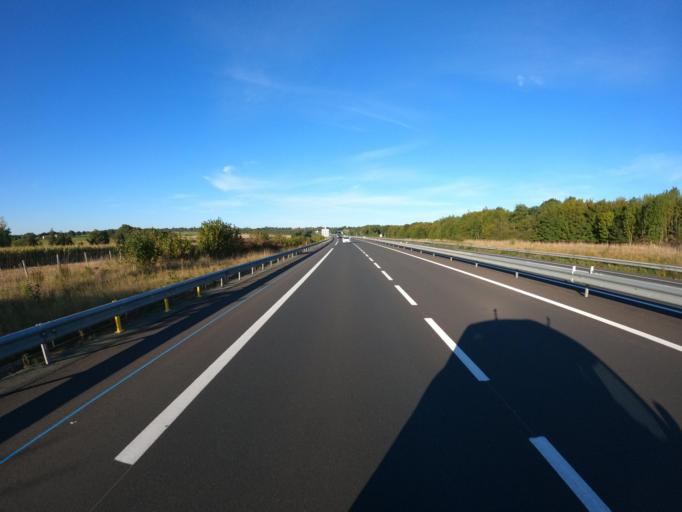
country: FR
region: Pays de la Loire
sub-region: Departement de la Vendee
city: La Gaubretiere
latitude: 46.9067
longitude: -1.0501
